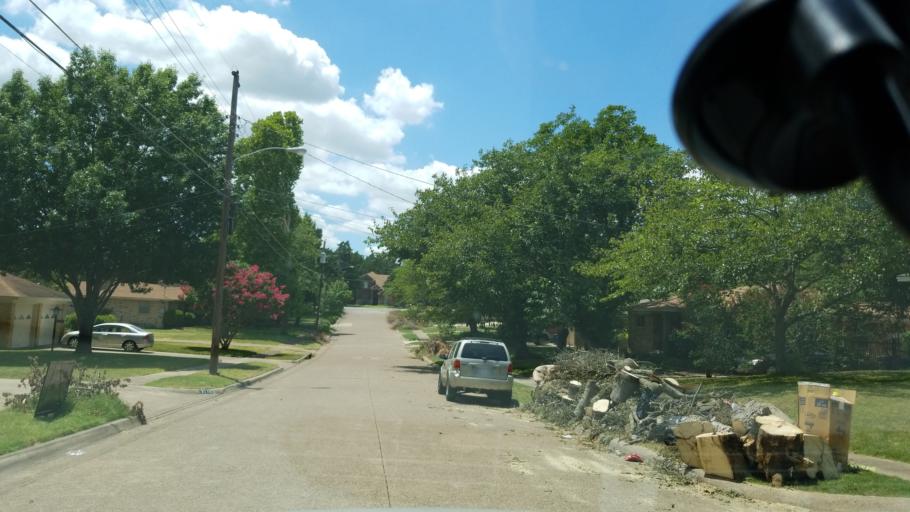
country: US
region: Texas
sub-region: Dallas County
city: Cockrell Hill
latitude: 32.6957
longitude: -96.8713
